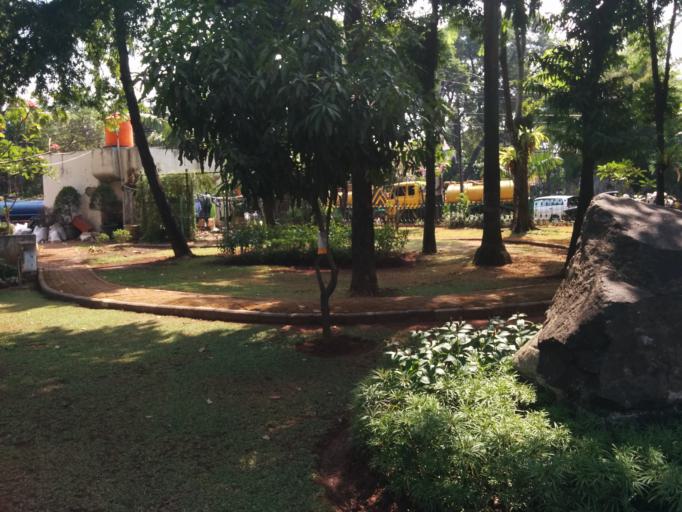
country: ID
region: Jakarta Raya
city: Jakarta
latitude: -6.2033
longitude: 106.8283
